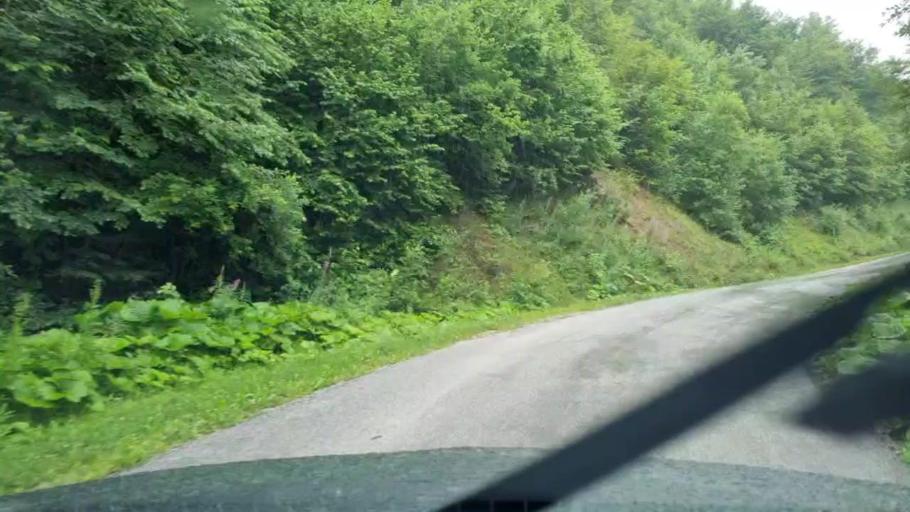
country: BA
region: Republika Srpska
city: Koran
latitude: 43.6633
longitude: 18.5903
